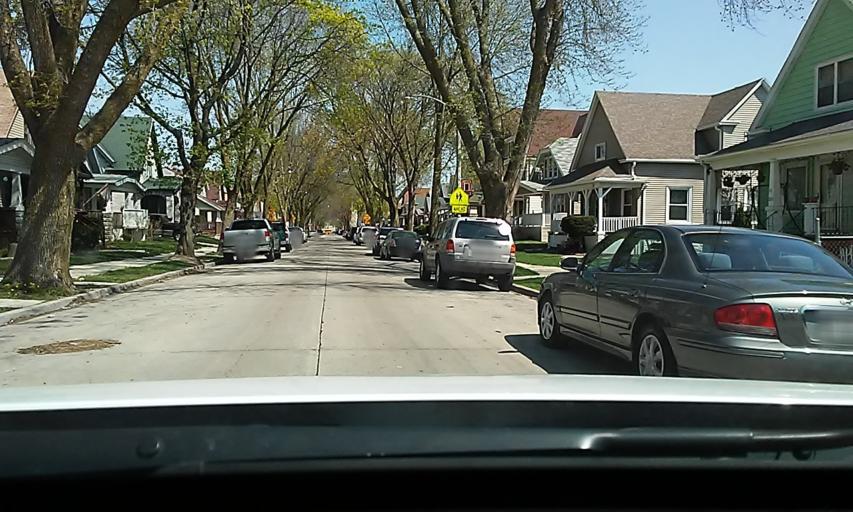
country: US
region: Wisconsin
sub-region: Milwaukee County
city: West Milwaukee
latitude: 43.0049
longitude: -87.9529
